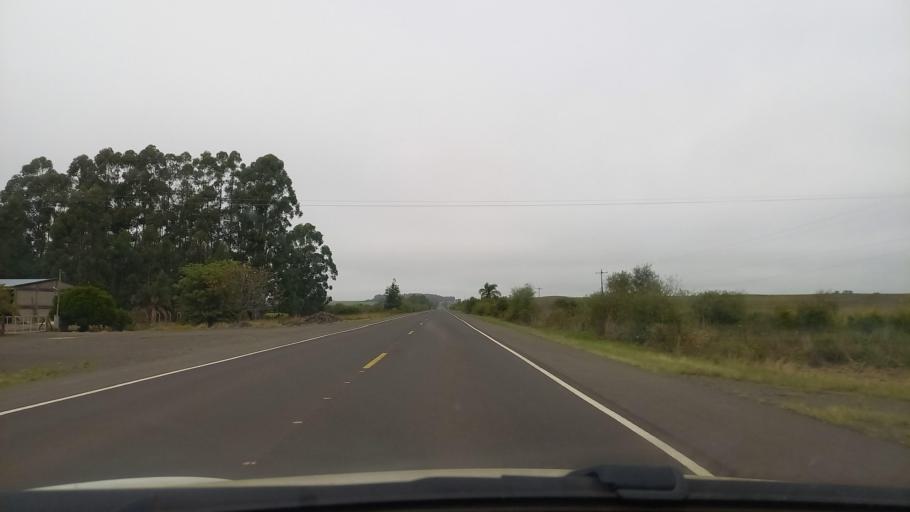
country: BR
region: Rio Grande do Sul
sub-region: Rosario Do Sul
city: Rosario do Sul
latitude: -30.3034
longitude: -54.9924
